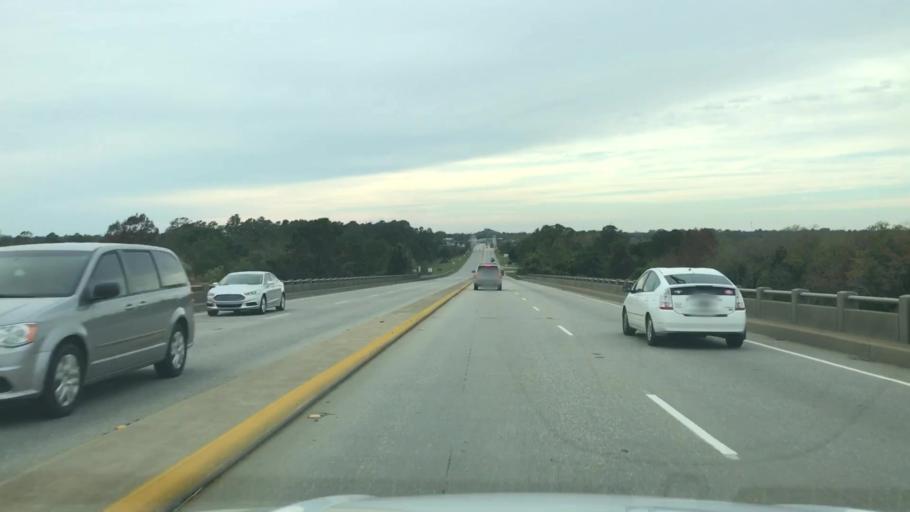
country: US
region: South Carolina
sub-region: Georgetown County
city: Georgetown
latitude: 33.3660
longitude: -79.2562
